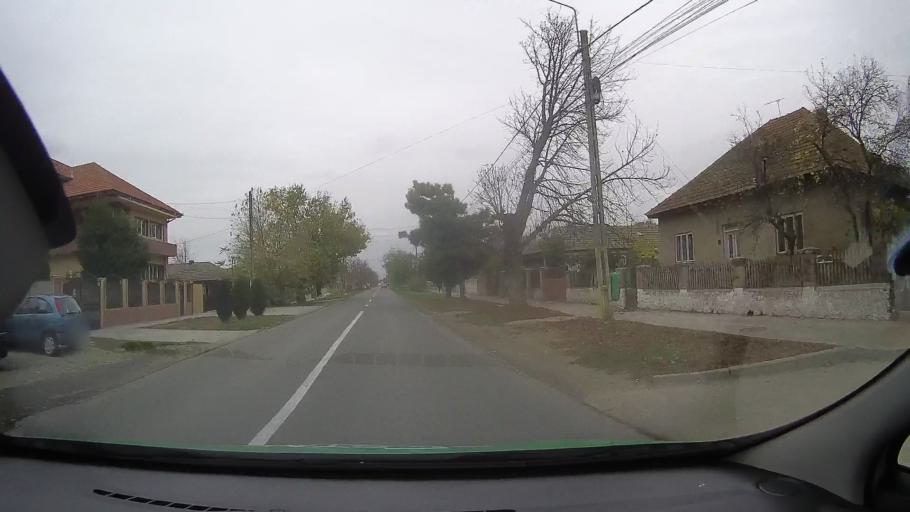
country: RO
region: Constanta
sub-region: Comuna Mihail Kogalniceanu
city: Mihail Kogalniceanu
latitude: 44.3673
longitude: 28.4624
